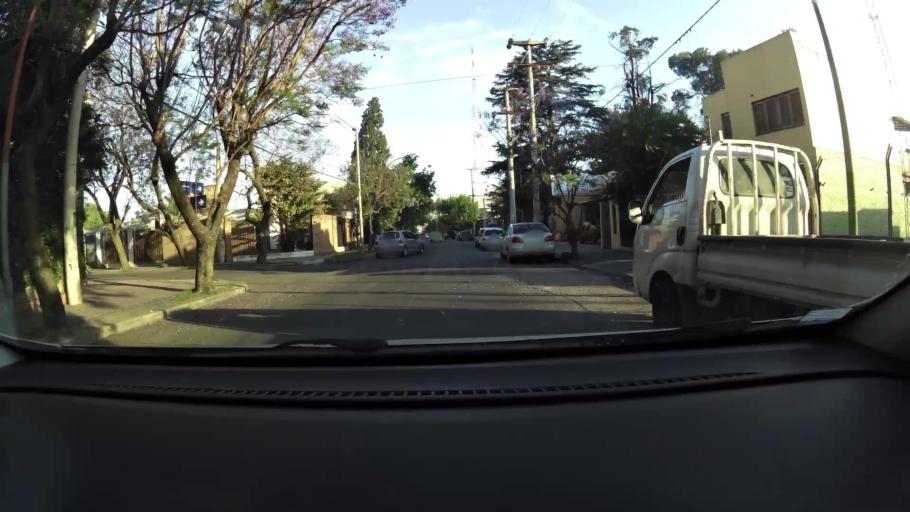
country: AR
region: Cordoba
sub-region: Departamento de Capital
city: Cordoba
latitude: -31.3785
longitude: -64.2281
